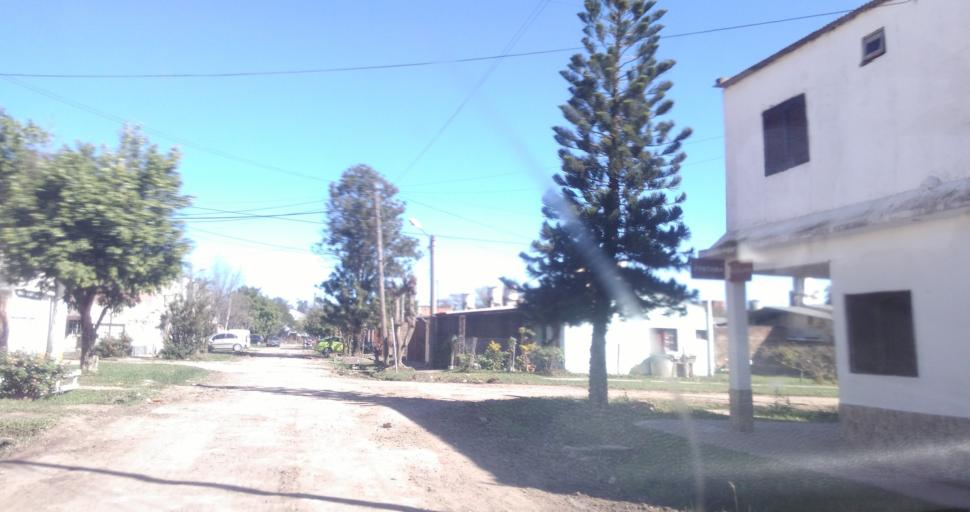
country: AR
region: Chaco
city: Fontana
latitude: -27.4396
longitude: -59.0185
